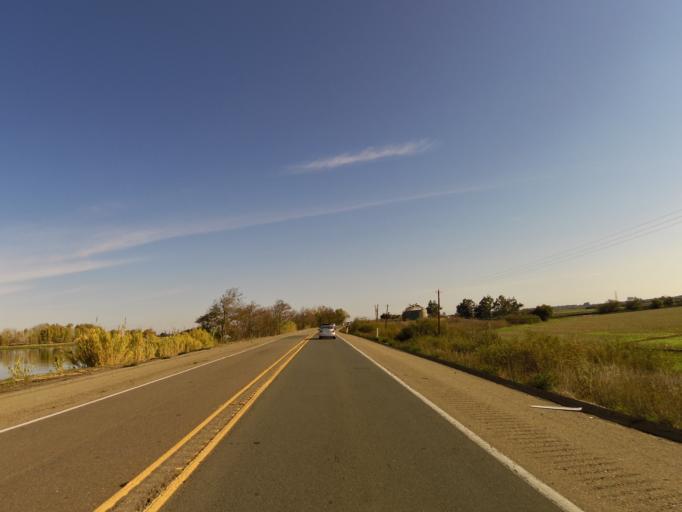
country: US
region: California
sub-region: Solano County
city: Rio Vista
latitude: 38.0807
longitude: -121.7234
